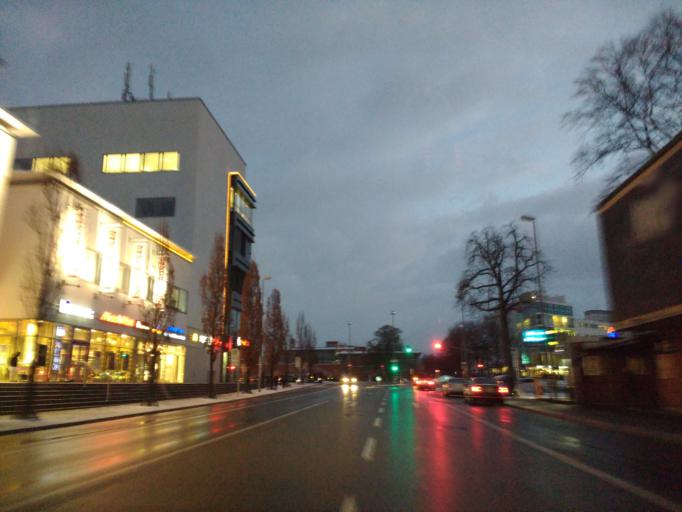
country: DE
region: Bavaria
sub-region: Swabia
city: Kempten (Allgaeu)
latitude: 47.7203
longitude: 10.3145
